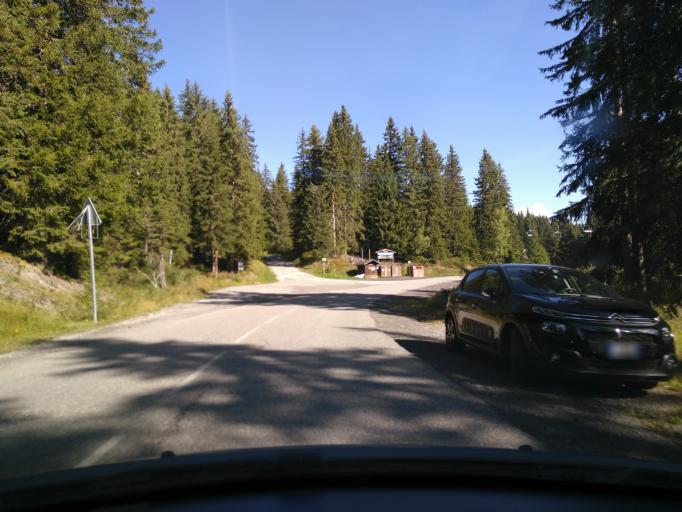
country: FR
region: Rhone-Alpes
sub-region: Departement de la Haute-Savoie
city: Praz-sur-Arly
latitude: 45.7801
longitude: 6.5267
